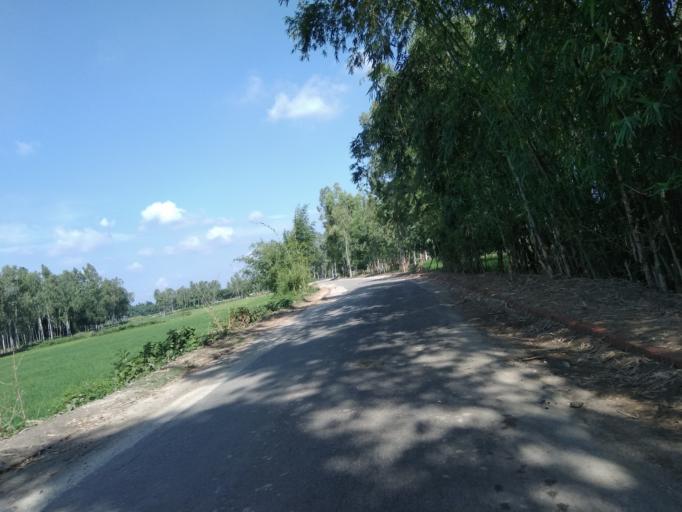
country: BD
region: Rangpur Division
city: Panchagarh
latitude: 26.2555
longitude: 88.6187
